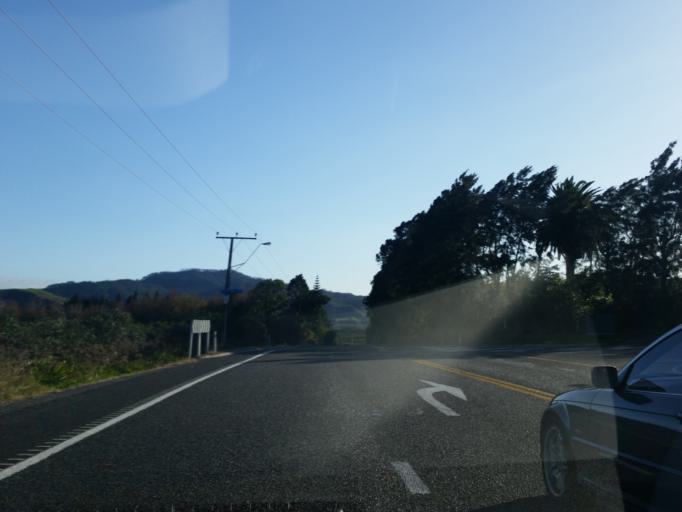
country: NZ
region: Bay of Plenty
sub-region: Western Bay of Plenty District
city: Katikati
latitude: -37.5195
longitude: 175.9196
